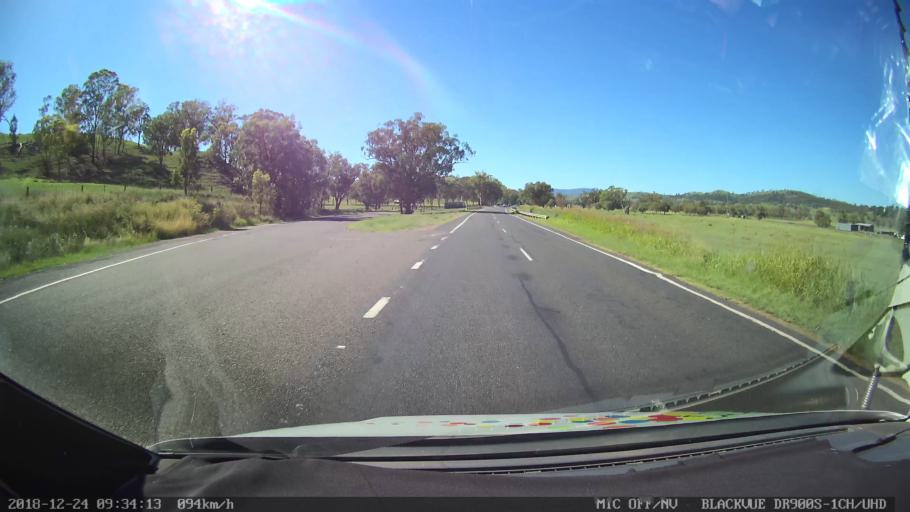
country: AU
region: New South Wales
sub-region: Liverpool Plains
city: Quirindi
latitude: -31.6120
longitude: 150.7142
